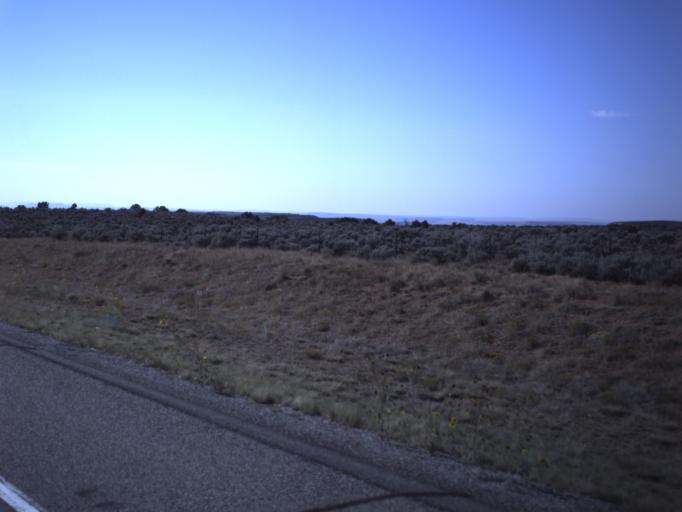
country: US
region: Utah
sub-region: San Juan County
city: Blanding
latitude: 37.5067
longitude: -109.4895
